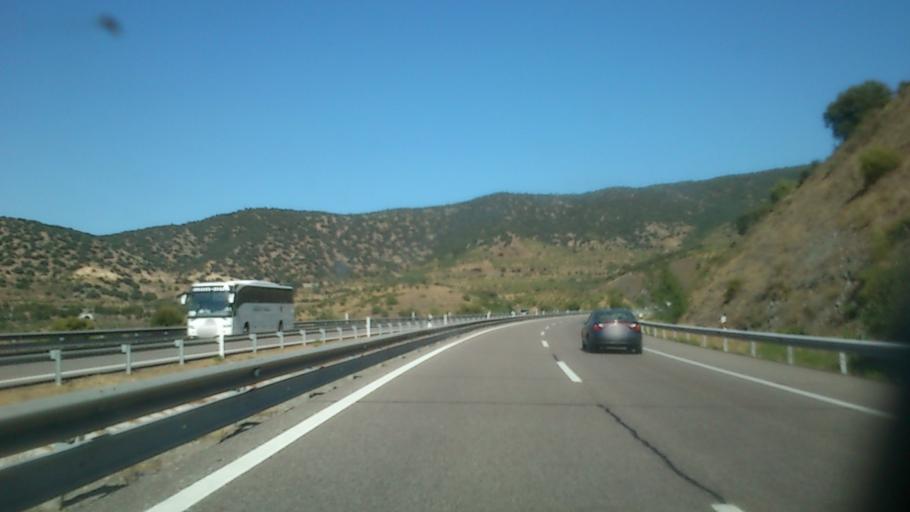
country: ES
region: Aragon
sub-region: Provincia de Zaragoza
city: Paracuellos de la Ribera
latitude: 41.4027
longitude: -1.5373
